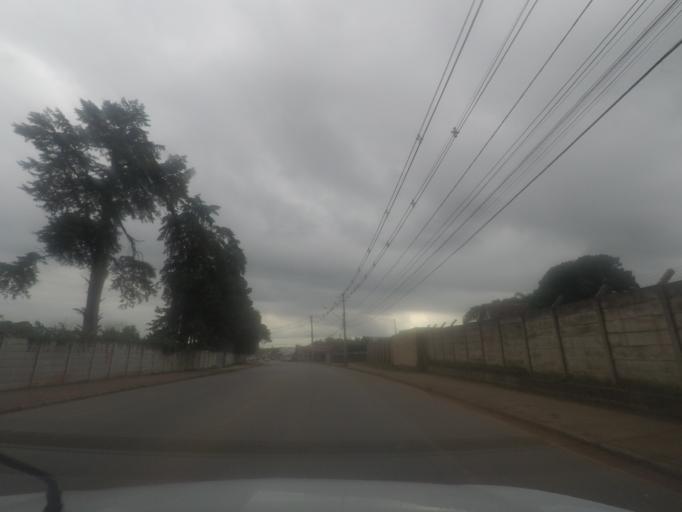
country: BR
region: Parana
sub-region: Sao Jose Dos Pinhais
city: Sao Jose dos Pinhais
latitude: -25.5590
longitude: -49.2607
